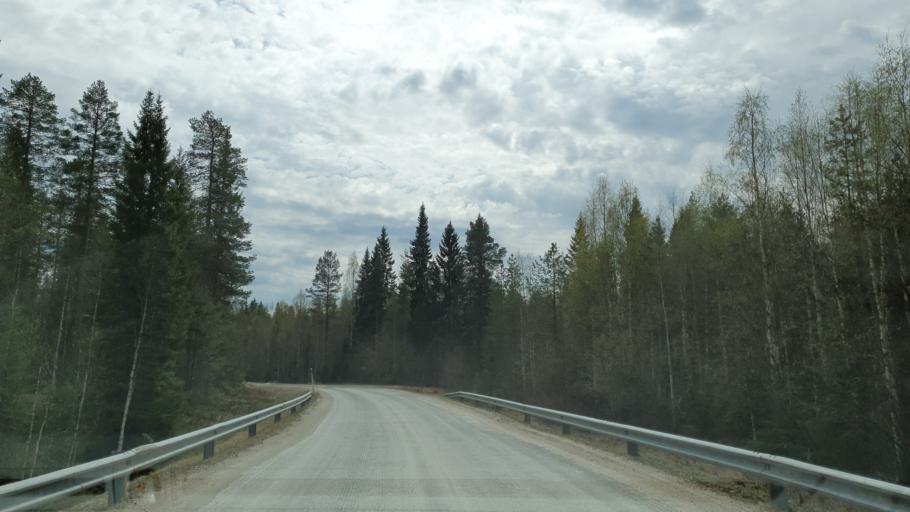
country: FI
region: Kainuu
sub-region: Kehys-Kainuu
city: Kuhmo
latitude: 64.1215
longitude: 29.9537
